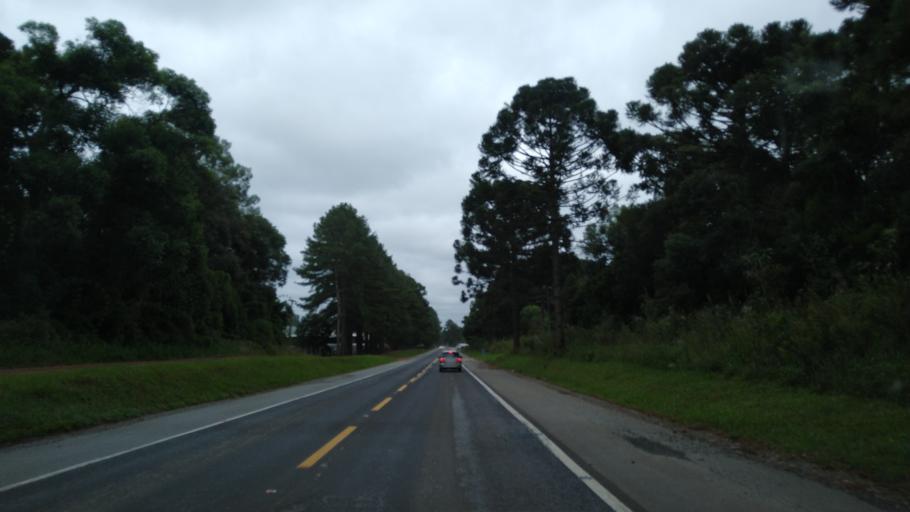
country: BR
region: Santa Catarina
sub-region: Tres Barras
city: Tres Barras
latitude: -26.1627
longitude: -50.1250
